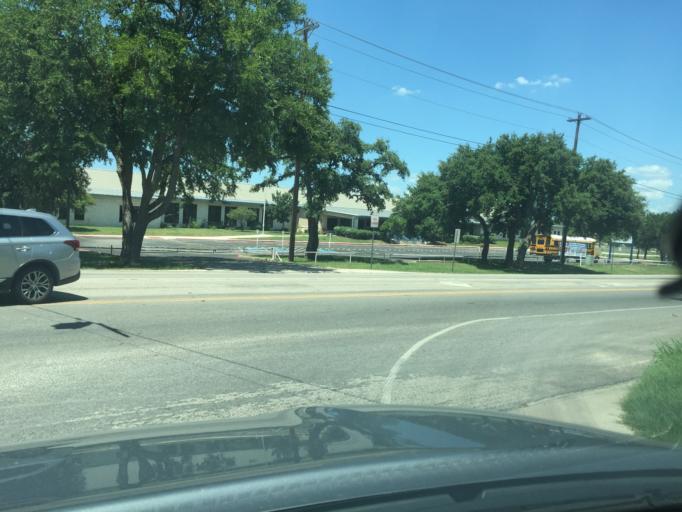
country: US
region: Texas
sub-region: Comal County
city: Bulverde
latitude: 29.7981
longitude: -98.4254
